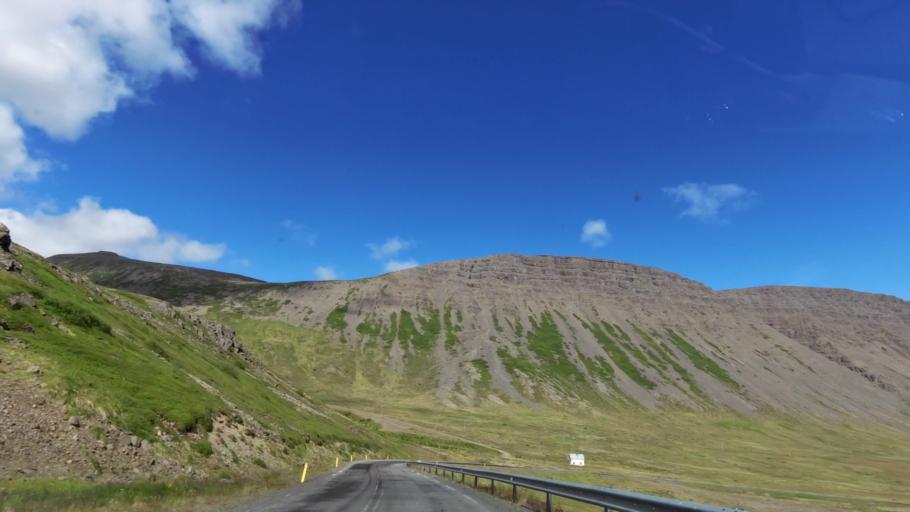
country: IS
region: Westfjords
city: Isafjoerdur
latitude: 65.6630
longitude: -23.6388
